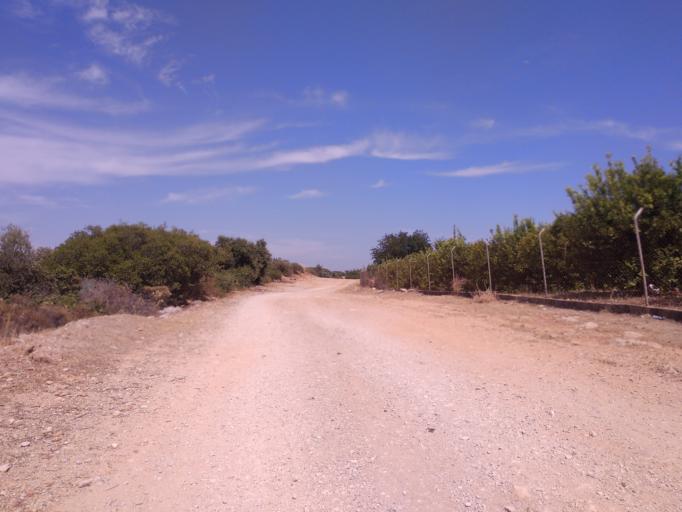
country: PT
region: Faro
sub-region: Faro
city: Santa Barbara de Nexe
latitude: 37.0923
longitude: -7.9676
